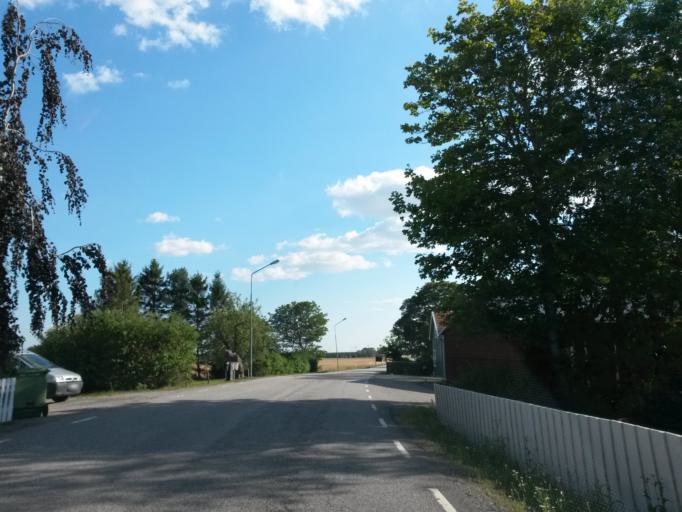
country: SE
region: Vaestra Goetaland
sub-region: Vara Kommun
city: Kvanum
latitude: 58.3705
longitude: 13.1473
